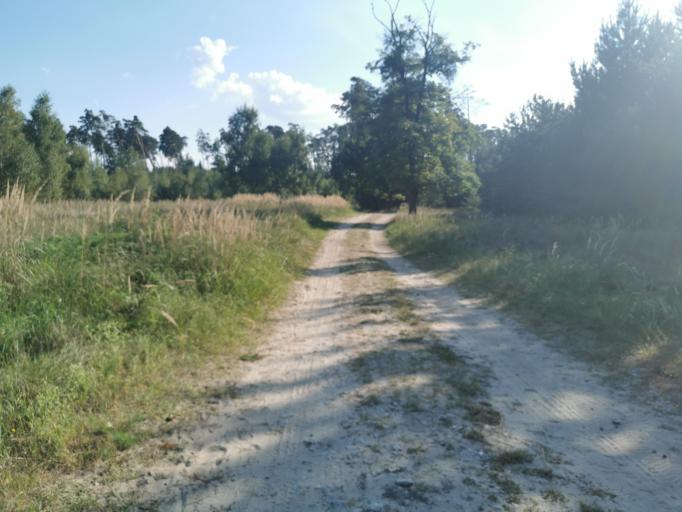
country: SK
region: Trnavsky
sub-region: Okres Senica
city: Senica
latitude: 48.6543
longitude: 17.2921
